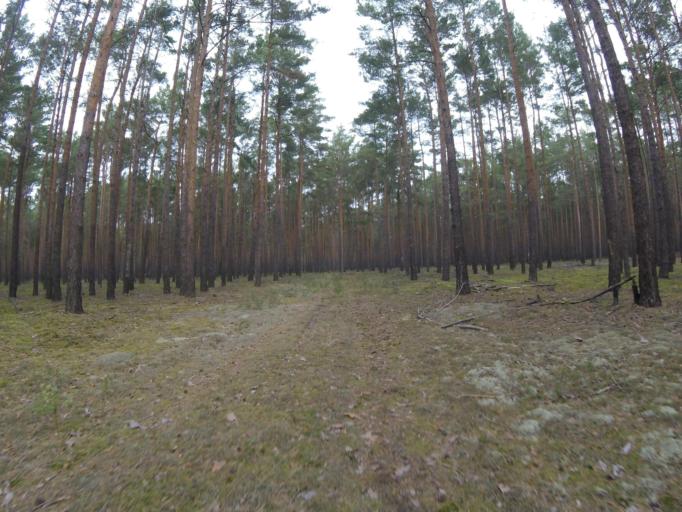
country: DE
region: Brandenburg
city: Gross Koris
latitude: 52.1913
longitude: 13.6833
